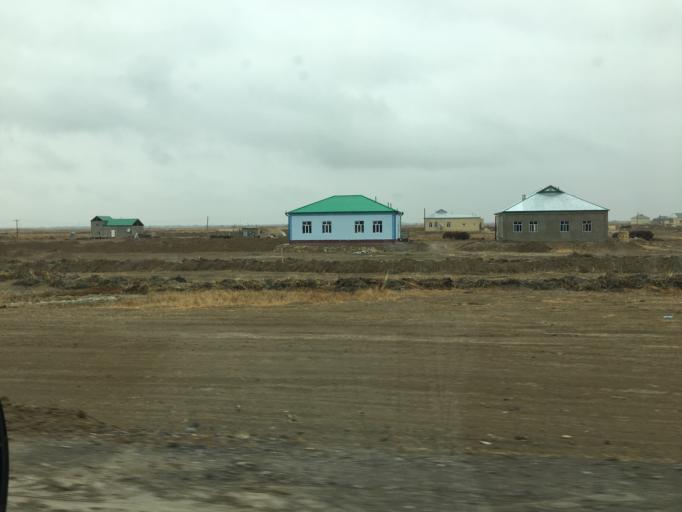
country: TM
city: Murgab
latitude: 37.4734
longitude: 62.0218
